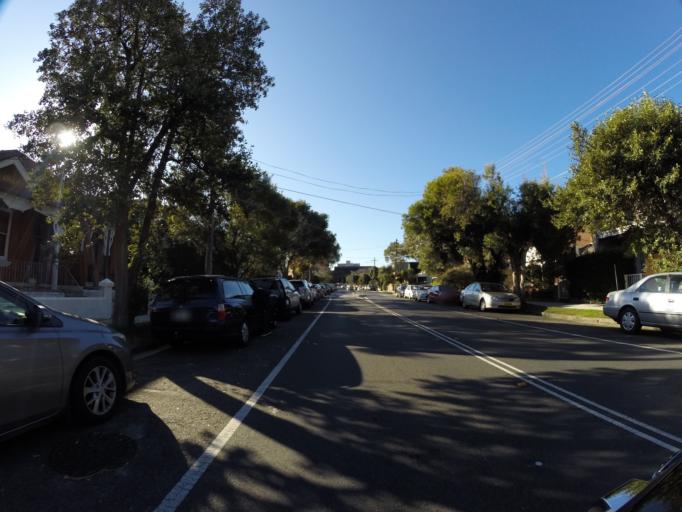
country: AU
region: New South Wales
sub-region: Waverley
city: Bondi
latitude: -33.8959
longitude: 151.2632
